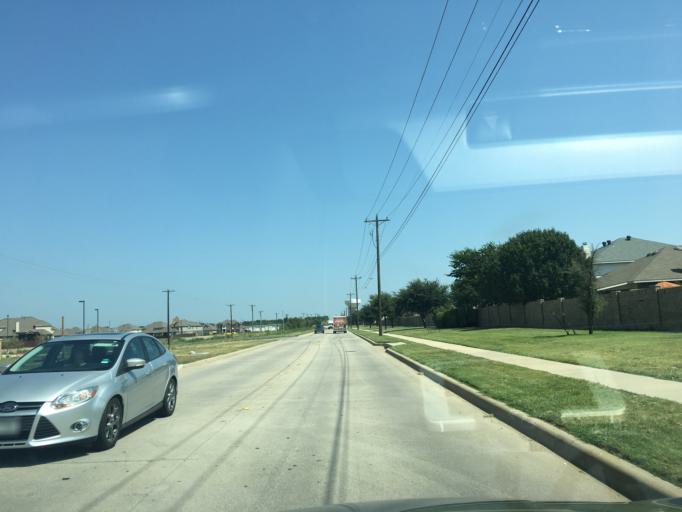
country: US
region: Texas
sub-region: Tarrant County
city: Blue Mound
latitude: 32.9156
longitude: -97.3315
